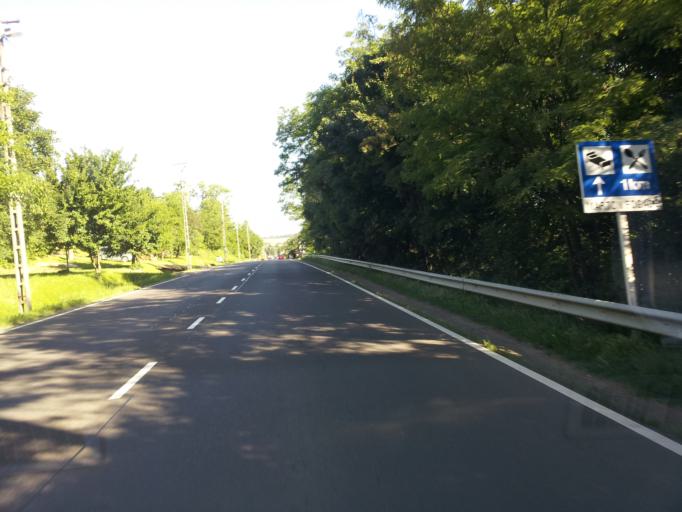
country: HU
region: Nograd
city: Nagyoroszi
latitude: 47.9975
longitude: 19.0964
